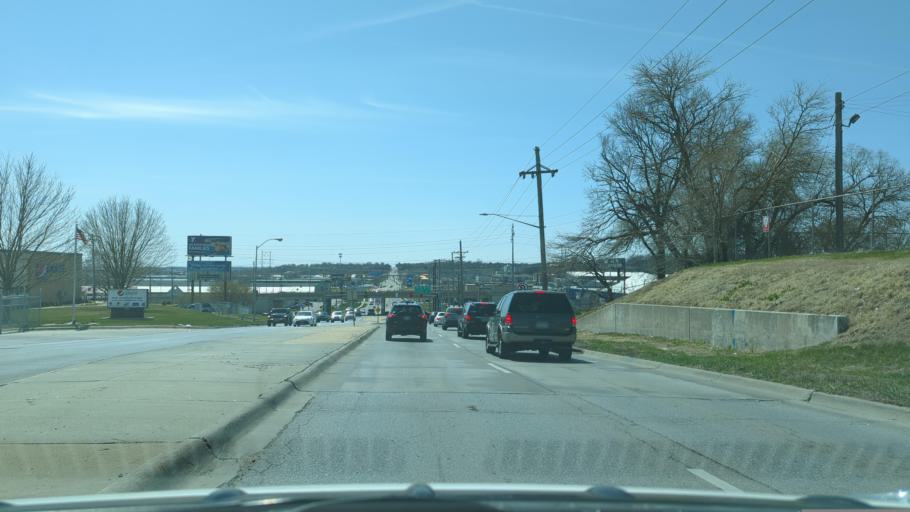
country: US
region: Nebraska
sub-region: Douglas County
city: Ralston
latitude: 41.2146
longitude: -96.0239
